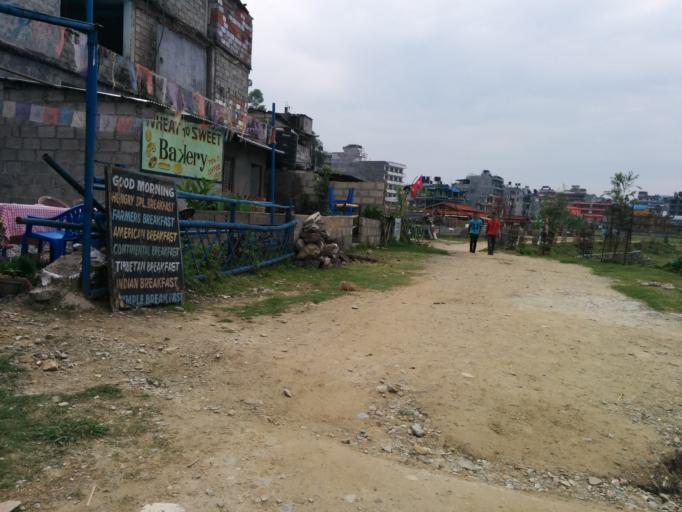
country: NP
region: Western Region
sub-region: Gandaki Zone
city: Pokhara
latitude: 28.2200
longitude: 83.9575
